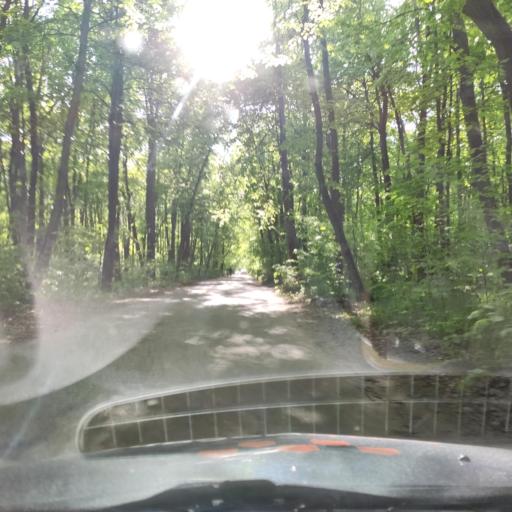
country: RU
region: Voronezj
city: Podgornoye
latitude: 51.7439
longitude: 39.2094
